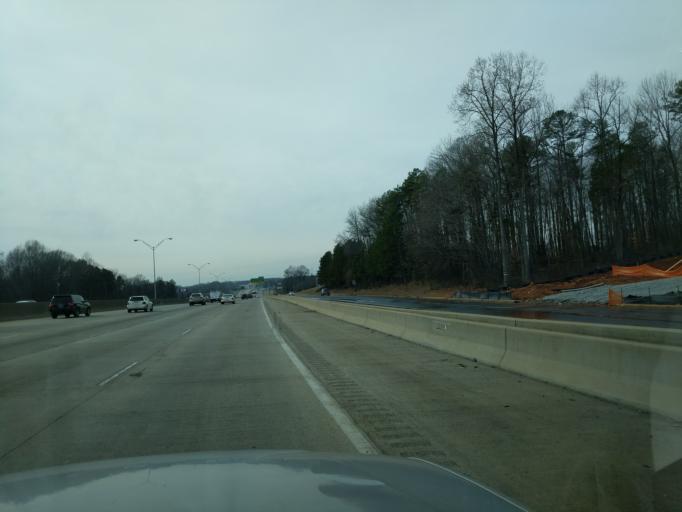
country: US
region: North Carolina
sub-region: Mecklenburg County
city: Charlotte
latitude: 35.2422
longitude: -80.9011
